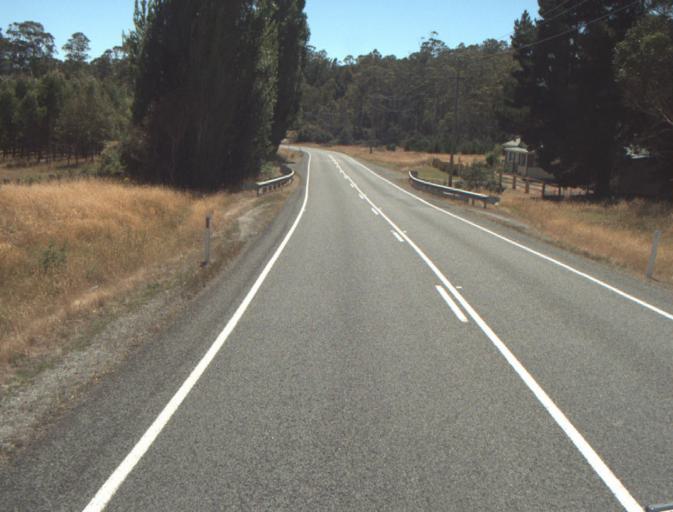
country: AU
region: Tasmania
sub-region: Launceston
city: Newstead
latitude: -41.3845
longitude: 147.3102
